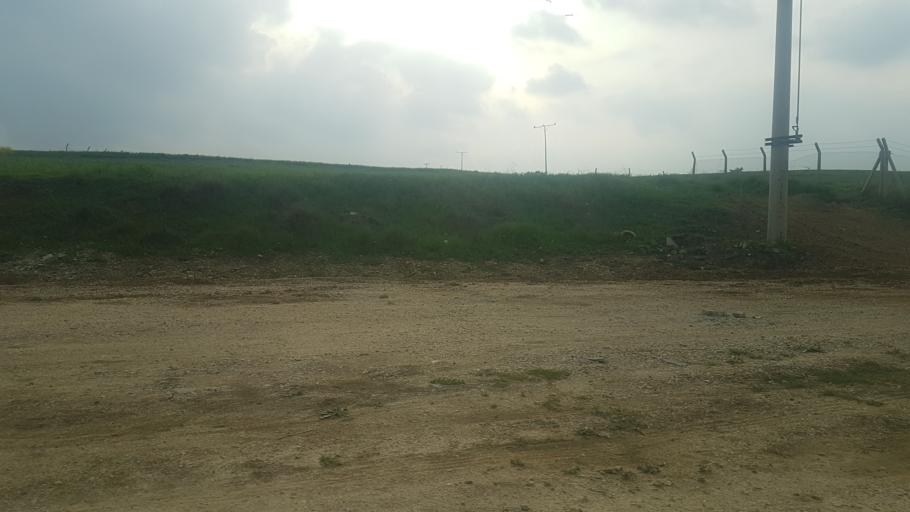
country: TR
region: Adana
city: Seyhan
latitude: 37.0498
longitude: 35.2094
